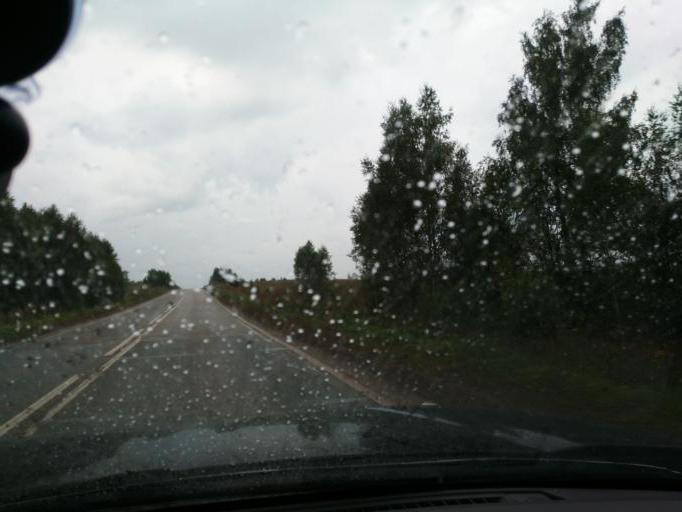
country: RU
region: Perm
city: Barda
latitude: 56.8661
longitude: 55.8995
